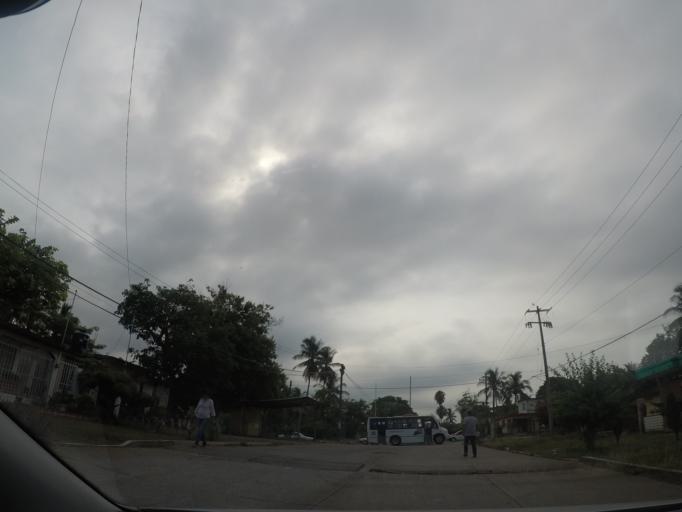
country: MX
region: Oaxaca
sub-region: Santa Maria Petapa
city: Llano Suchiapa
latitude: 16.8712
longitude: -95.0475
